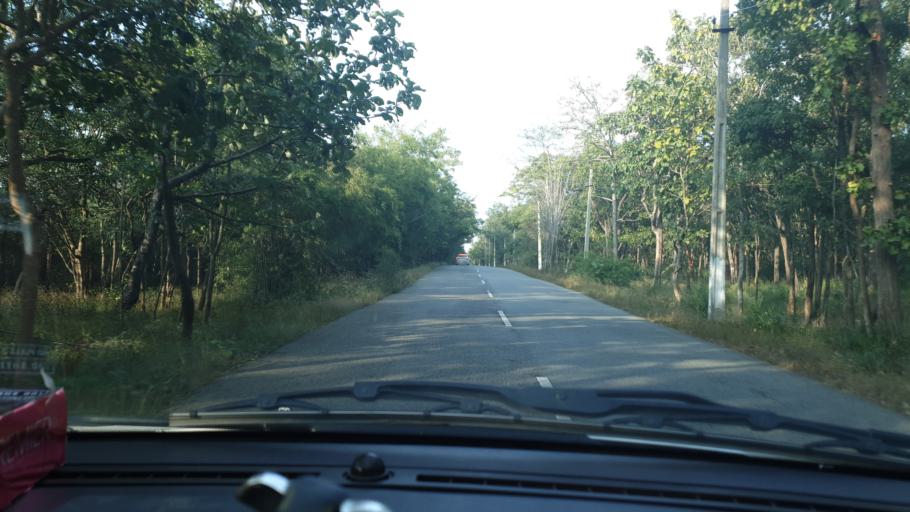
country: IN
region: Andhra Pradesh
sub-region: Kurnool
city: Srisailam
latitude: 16.2998
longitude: 78.7313
